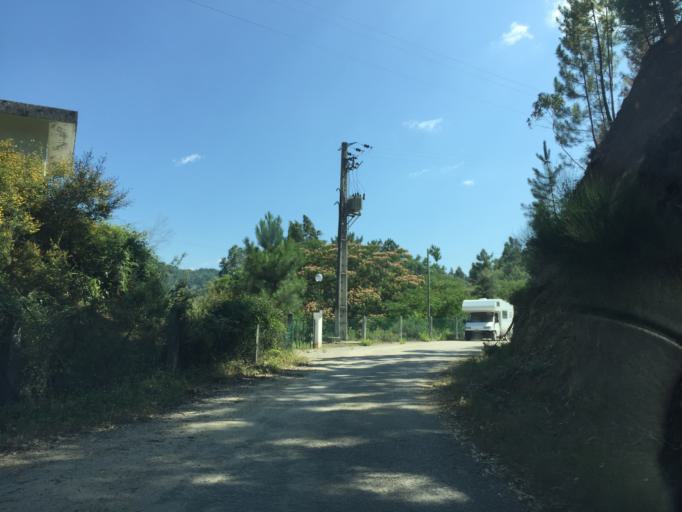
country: PT
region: Leiria
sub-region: Pedrogao Grande
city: Pedrogao Grande
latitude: 39.9274
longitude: -8.1323
